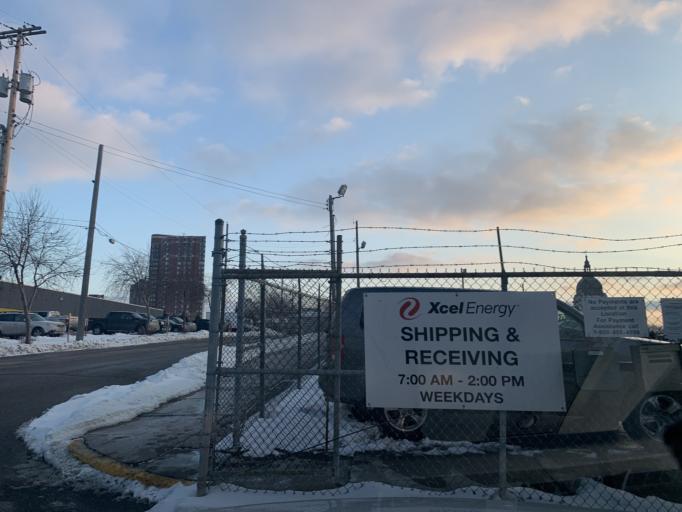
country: US
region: Minnesota
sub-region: Hennepin County
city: Minneapolis
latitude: 44.9770
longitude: -93.2843
